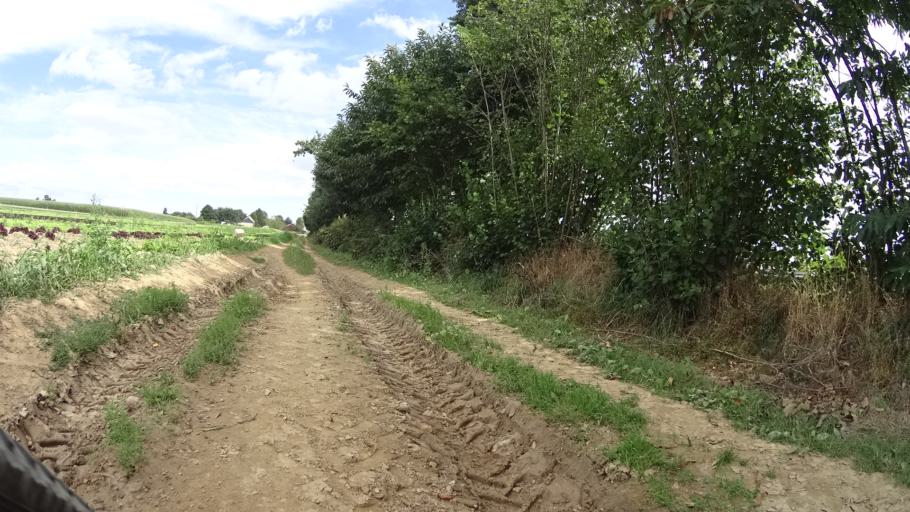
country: FR
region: Brittany
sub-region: Departement d'Ille-et-Vilaine
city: Vignoc
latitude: 48.2352
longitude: -1.7828
